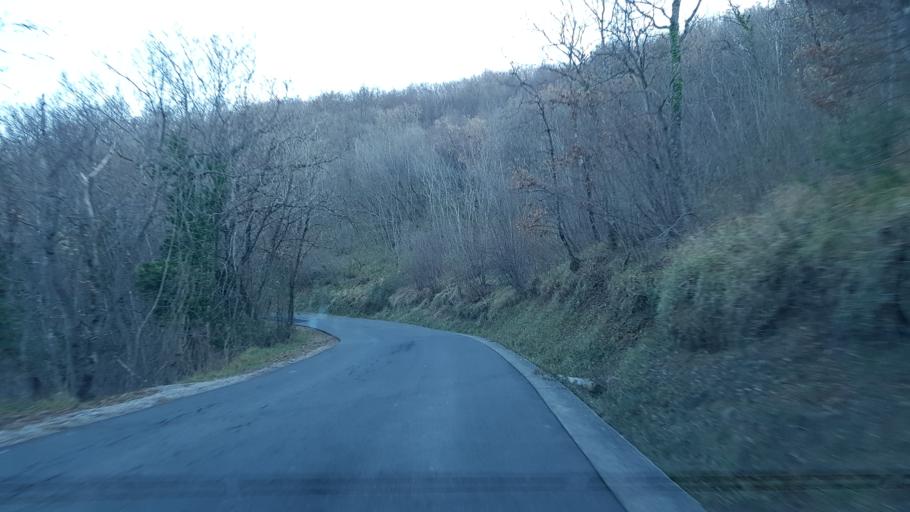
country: SI
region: Koper-Capodistria
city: Pobegi
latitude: 45.4932
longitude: 13.7918
